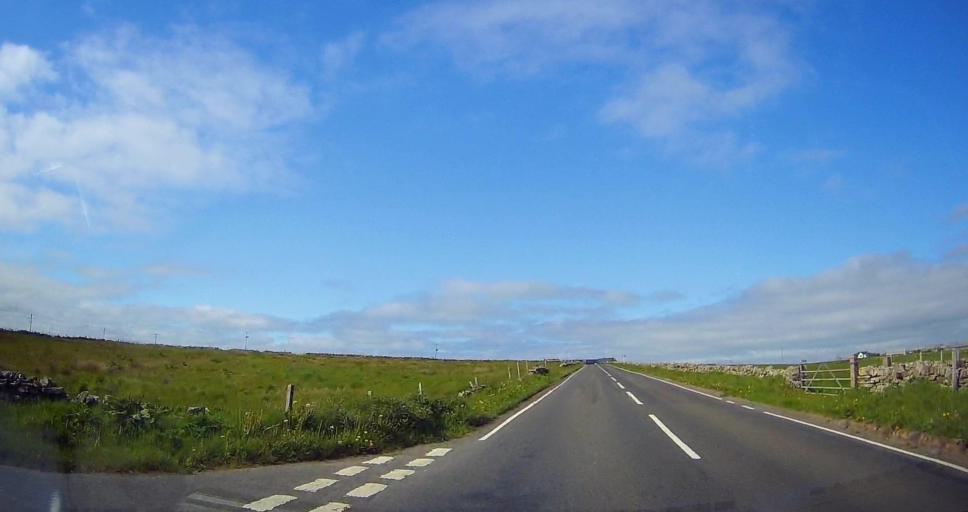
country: GB
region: Scotland
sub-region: Orkney Islands
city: Kirkwall
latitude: 58.9637
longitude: -2.9420
